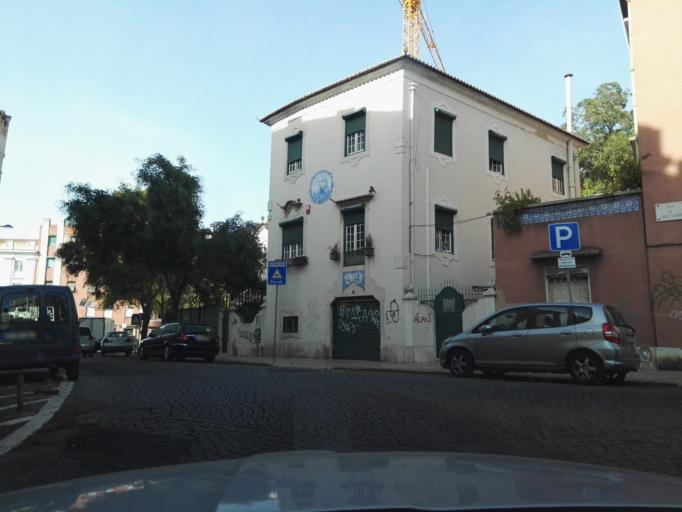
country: PT
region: Lisbon
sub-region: Lisbon
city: Lisbon
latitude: 38.7256
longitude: -9.1323
